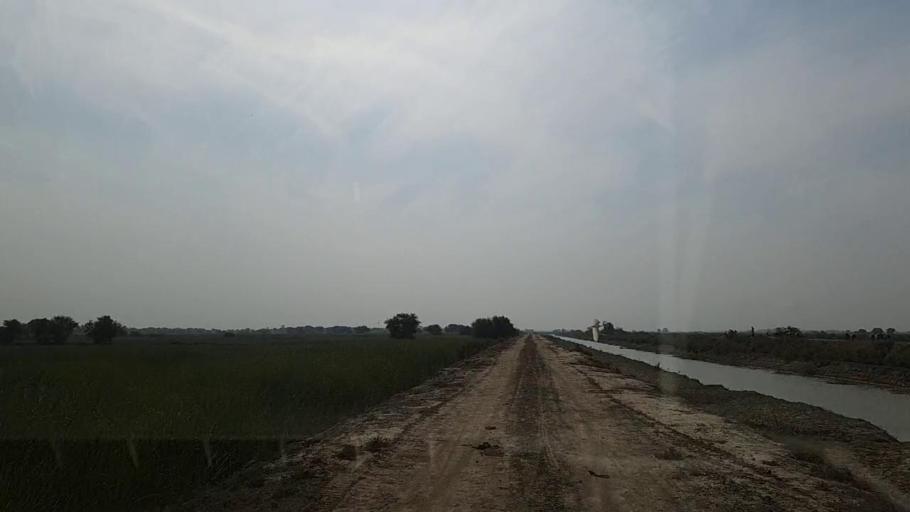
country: PK
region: Sindh
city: Mirpur Batoro
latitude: 24.6698
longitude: 68.2499
